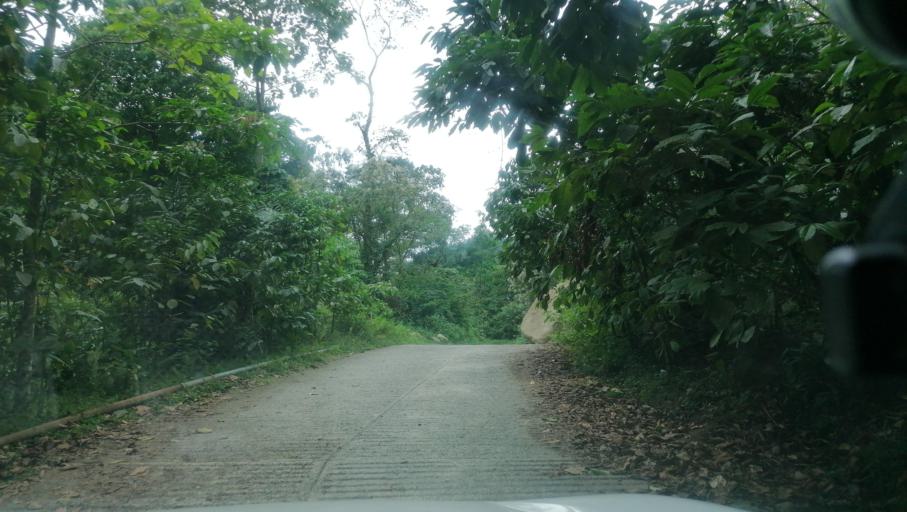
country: MX
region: Chiapas
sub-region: Cacahoatan
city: Benito Juarez
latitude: 15.1010
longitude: -92.1867
